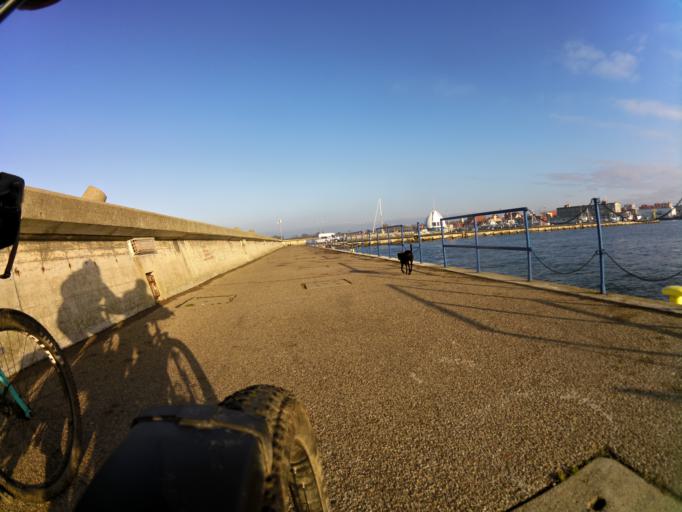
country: PL
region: Pomeranian Voivodeship
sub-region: Powiat pucki
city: Hel
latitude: 54.6007
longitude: 18.7993
